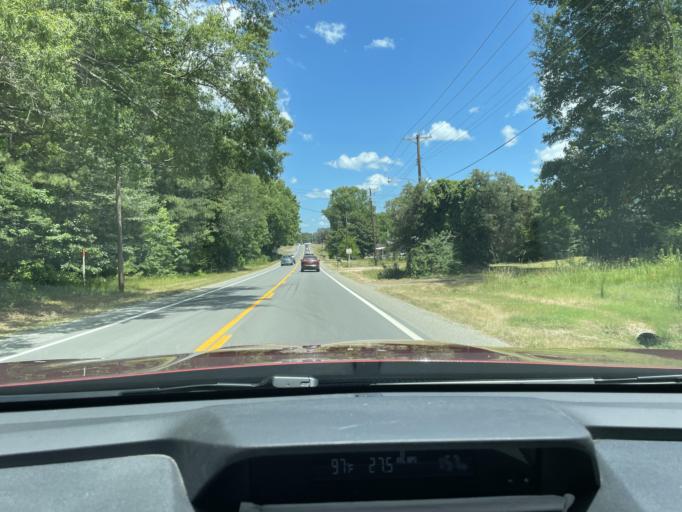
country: US
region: Arkansas
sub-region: Drew County
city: Monticello
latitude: 33.6285
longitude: -91.7738
